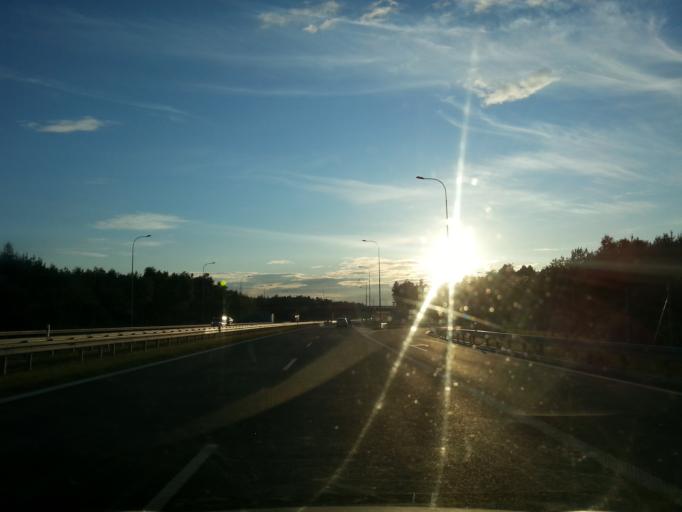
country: PL
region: Lodz Voivodeship
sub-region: Powiat wieruszowski
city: Wieruszow
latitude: 51.3068
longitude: 18.1903
